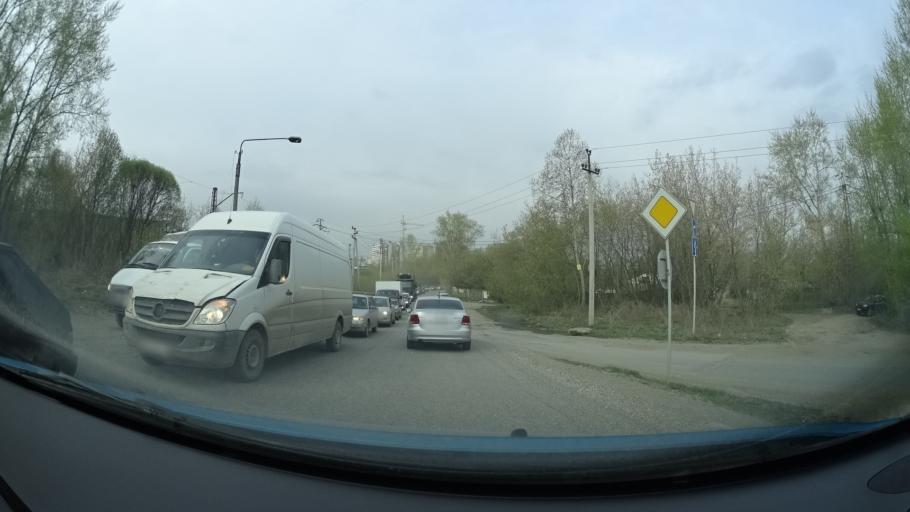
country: RU
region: Perm
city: Kondratovo
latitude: 58.0031
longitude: 56.1633
